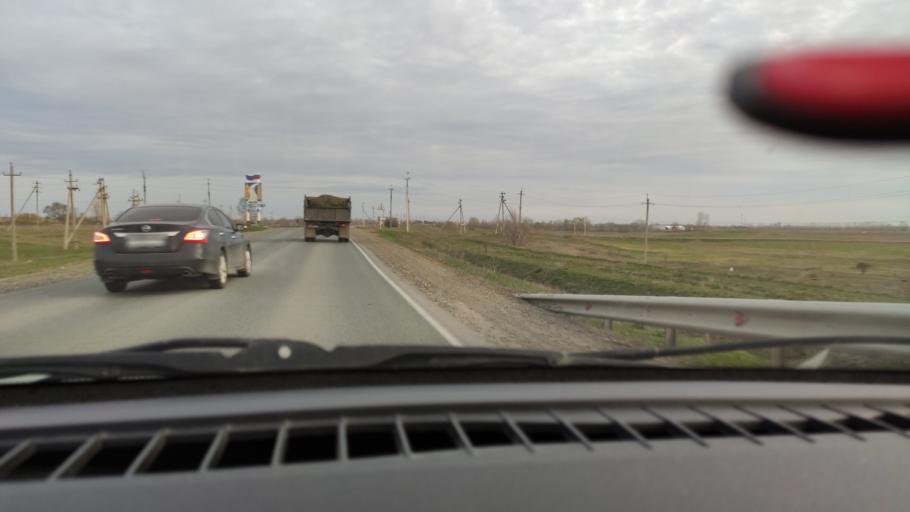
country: RU
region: Orenburg
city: Tatarskaya Kargala
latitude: 51.9143
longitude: 55.1733
